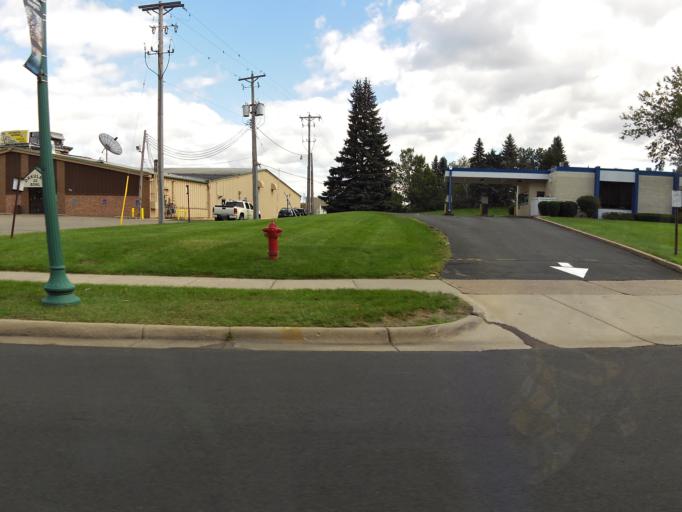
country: US
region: Minnesota
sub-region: Dakota County
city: Inver Grove Heights
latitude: 44.8514
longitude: -93.0447
